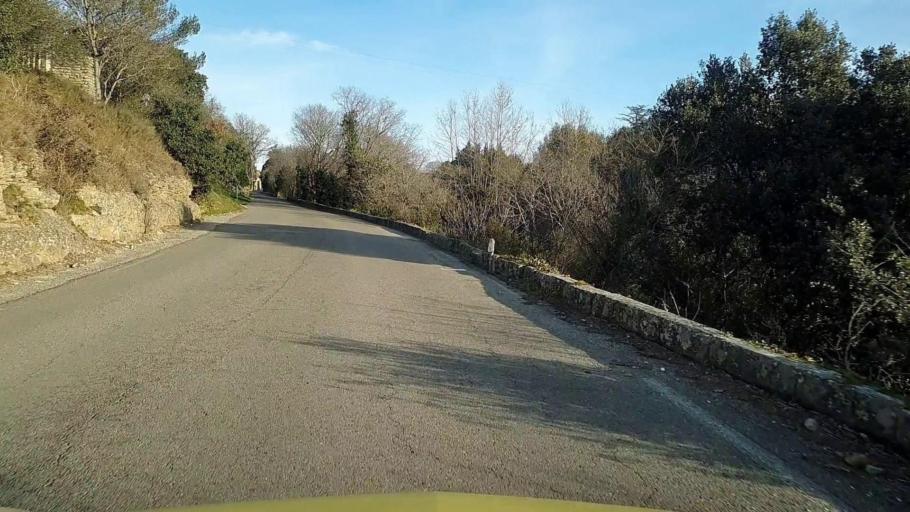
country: FR
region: Languedoc-Roussillon
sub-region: Departement du Gard
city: Castillon-du-Gard
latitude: 43.9663
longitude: 4.5550
